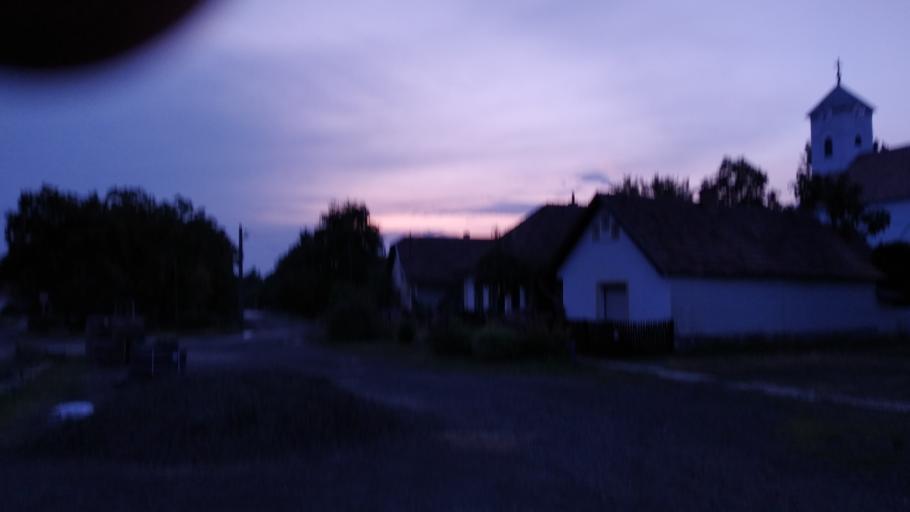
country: HU
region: Pest
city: Szob
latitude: 47.9358
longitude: 18.8292
